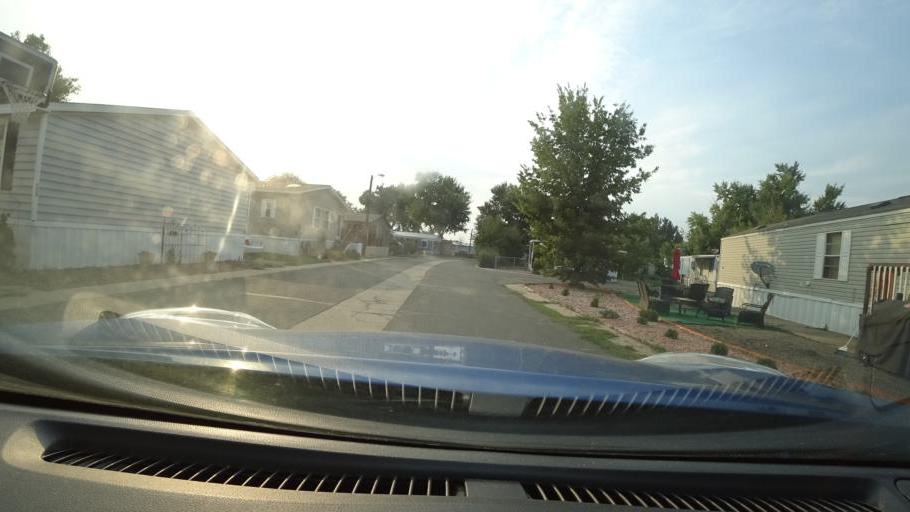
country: US
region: Colorado
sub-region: Adams County
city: Aurora
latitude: 39.7416
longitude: -104.7894
